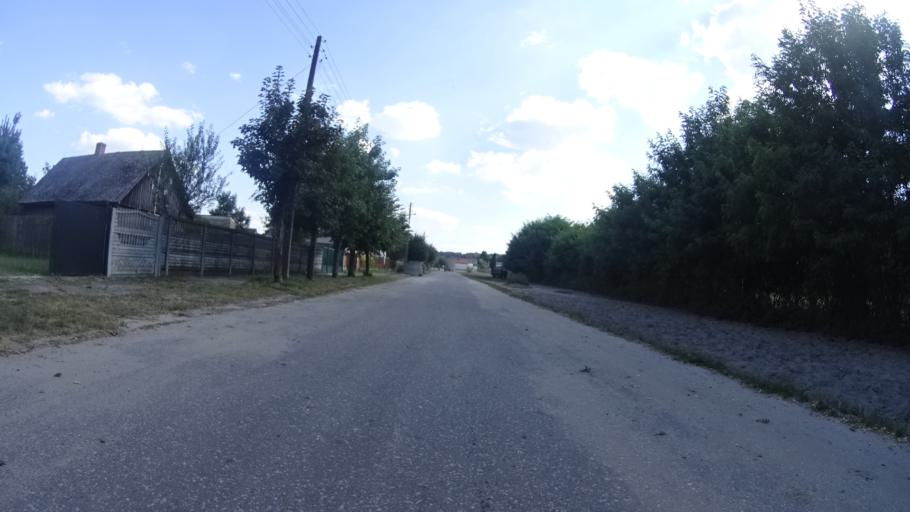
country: PL
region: Masovian Voivodeship
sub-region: Powiat bialobrzeski
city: Wysmierzyce
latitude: 51.6280
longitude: 20.8173
